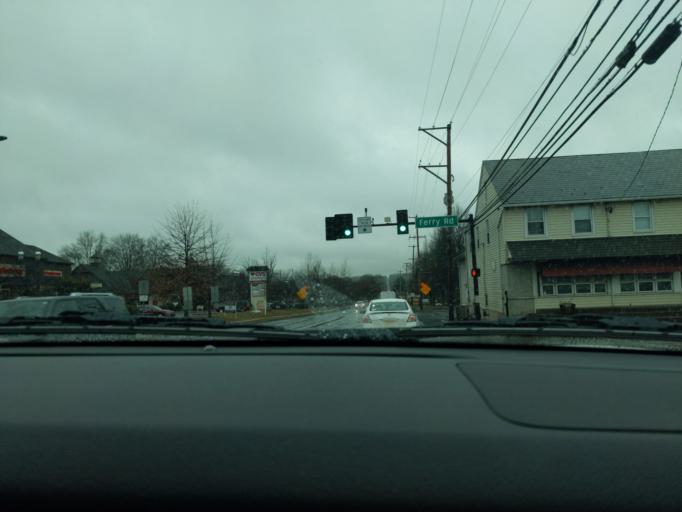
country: US
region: Pennsylvania
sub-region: Bucks County
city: Doylestown
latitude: 40.3412
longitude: -75.1509
